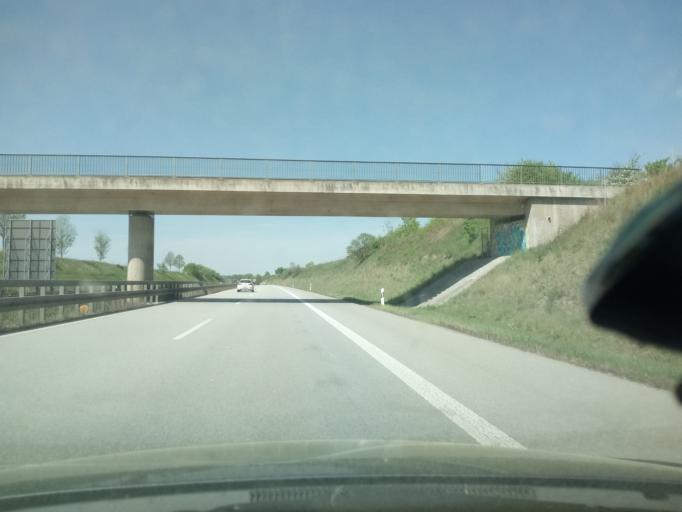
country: DE
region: Bavaria
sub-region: Upper Bavaria
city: Aresing
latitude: 48.2707
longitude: 12.5969
